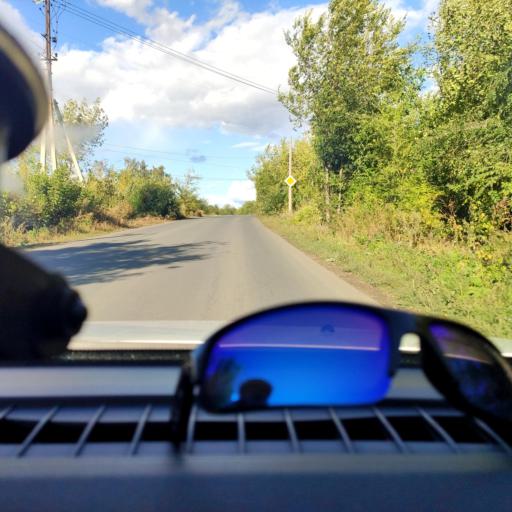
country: RU
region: Samara
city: Chapayevsk
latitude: 52.9921
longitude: 49.7305
